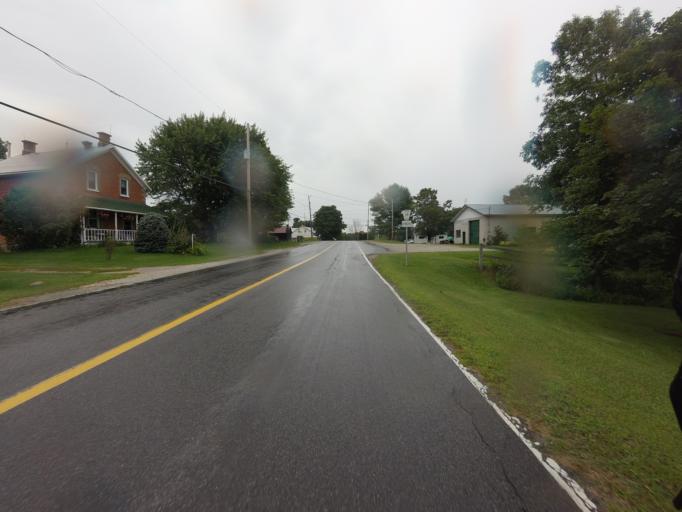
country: CA
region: Ontario
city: Perth
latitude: 44.9574
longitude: -76.3932
